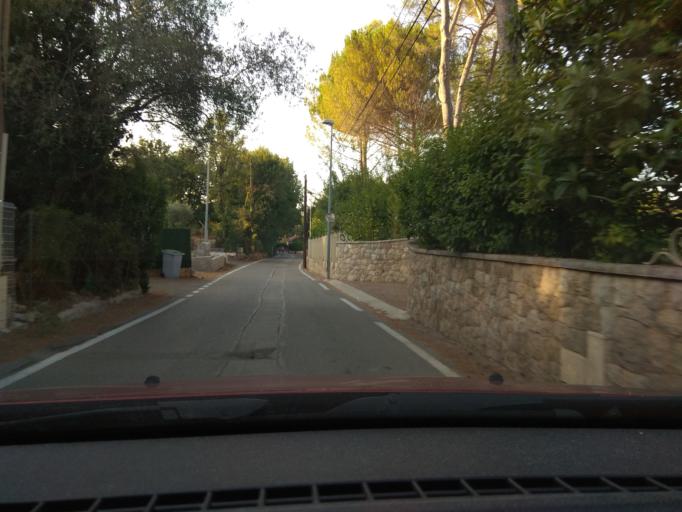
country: FR
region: Provence-Alpes-Cote d'Azur
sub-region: Departement des Alpes-Maritimes
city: Le Rouret
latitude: 43.6721
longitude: 7.0466
